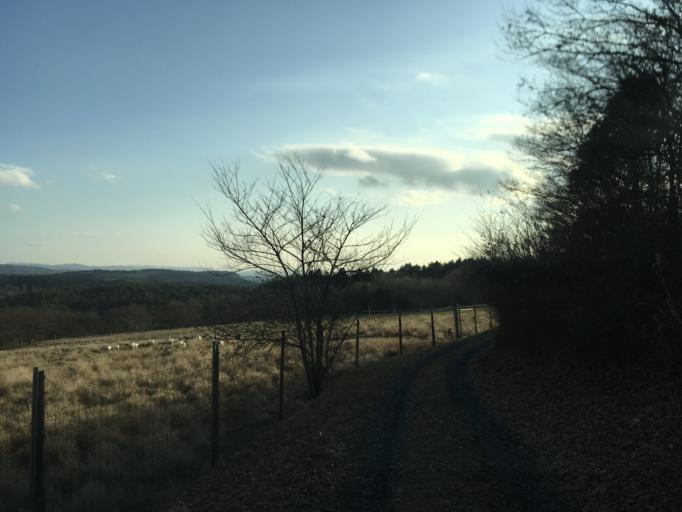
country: JP
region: Iwate
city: Ichinoseki
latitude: 38.8188
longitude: 141.2635
